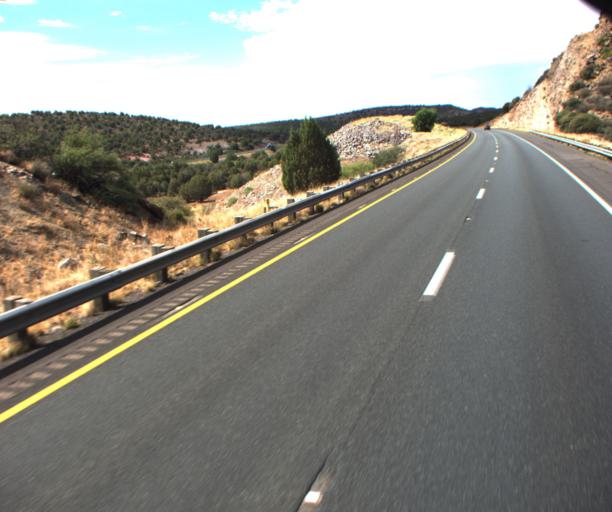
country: US
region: Arizona
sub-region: Yavapai County
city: Camp Verde
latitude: 34.5011
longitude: -112.0029
